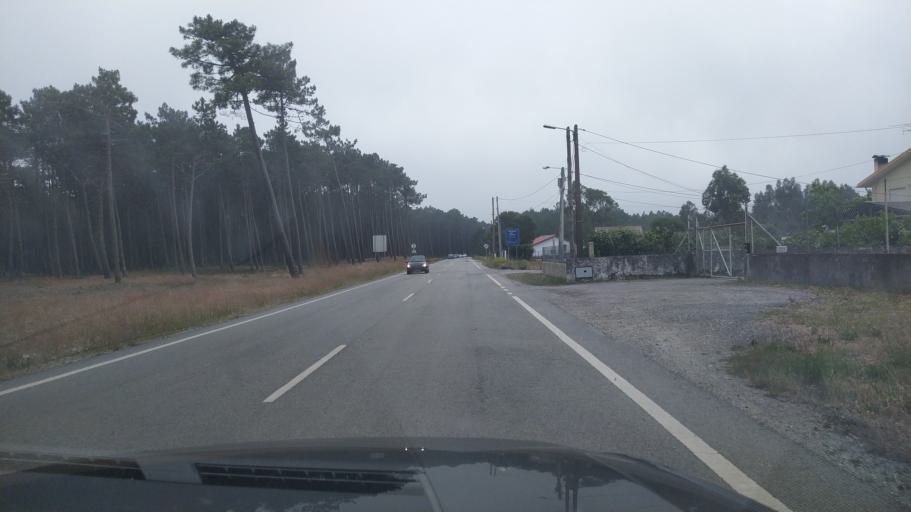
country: PT
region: Aveiro
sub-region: Ilhavo
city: Gafanha da Encarnacao
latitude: 40.5983
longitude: -8.7238
